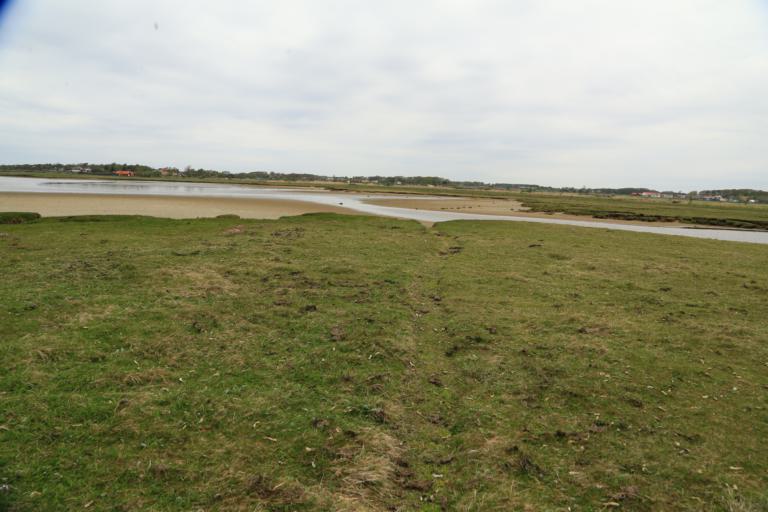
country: SE
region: Halland
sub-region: Varbergs Kommun
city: Traslovslage
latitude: 57.0328
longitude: 12.3166
